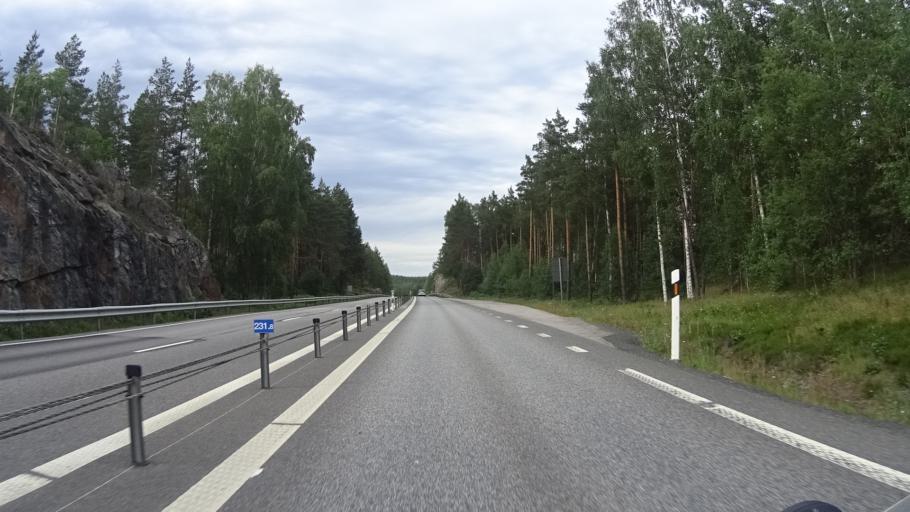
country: SE
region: OEstergoetland
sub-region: Valdemarsviks Kommun
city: Valdemarsvik
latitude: 58.1023
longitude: 16.5391
